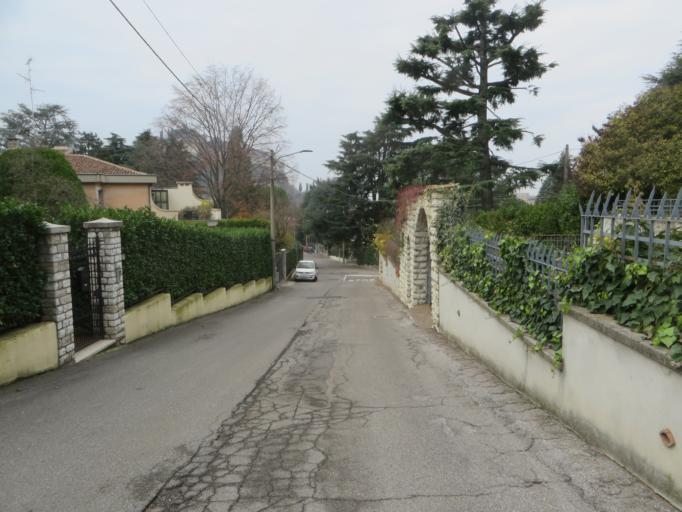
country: IT
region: Lombardy
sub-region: Provincia di Brescia
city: Brescia
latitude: 45.5448
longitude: 10.2328
